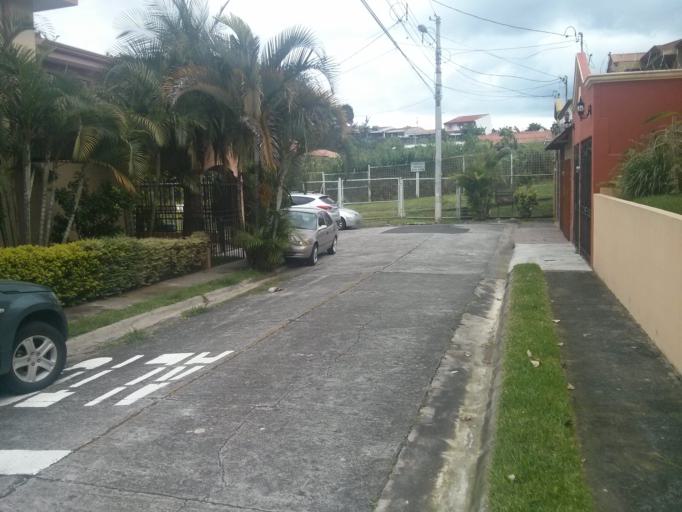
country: CR
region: San Jose
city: Curridabat
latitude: 9.9017
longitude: -84.0533
